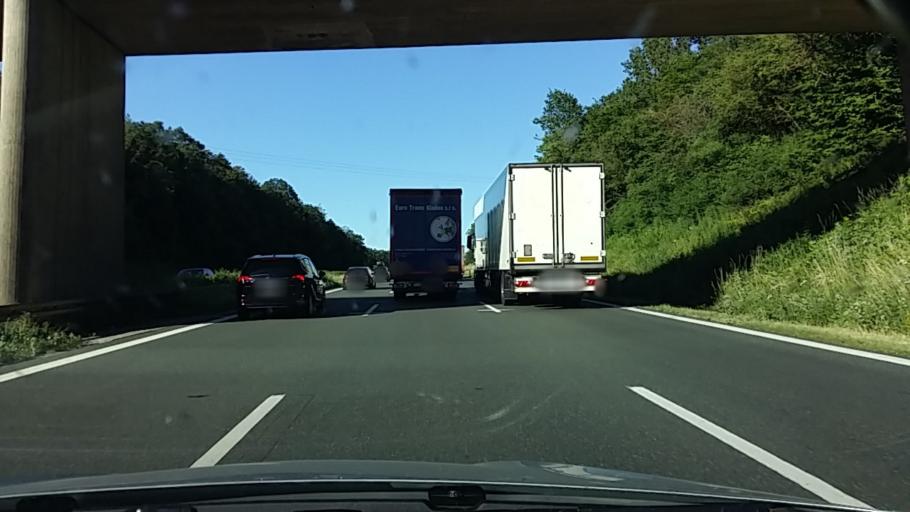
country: DE
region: Bavaria
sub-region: Regierungsbezirk Mittelfranken
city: Petersaurach
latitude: 49.2886
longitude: 10.7312
